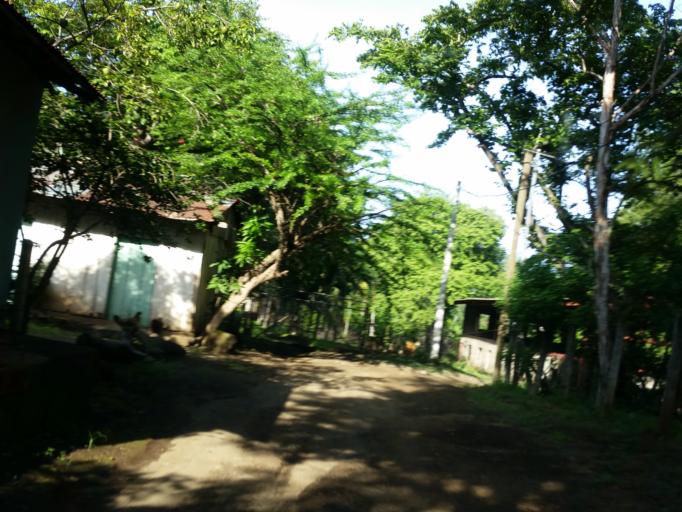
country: NI
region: Managua
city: Managua
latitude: 12.0789
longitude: -86.2266
